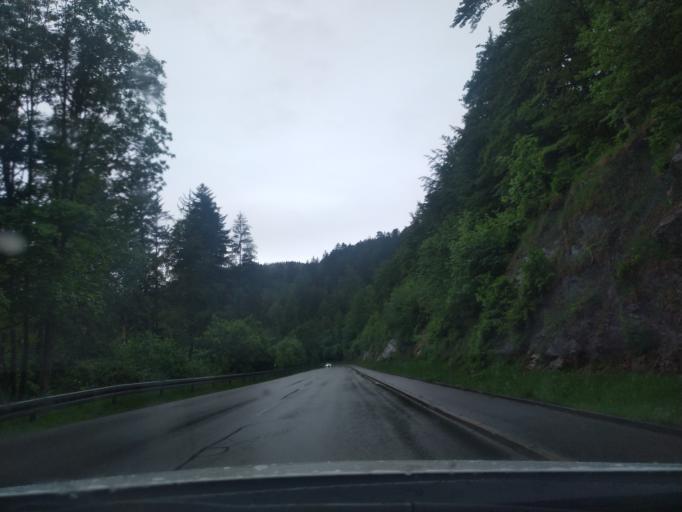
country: DE
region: Baden-Wuerttemberg
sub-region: Freiburg Region
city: Hausern
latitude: 47.7558
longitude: 8.1510
